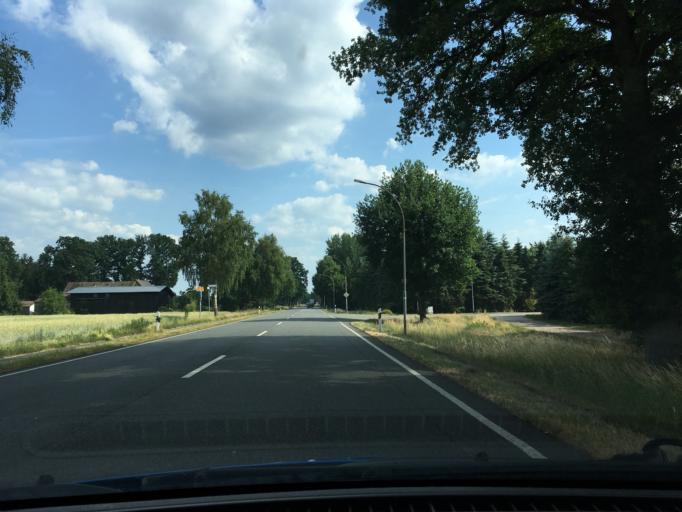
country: DE
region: Lower Saxony
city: Handeloh
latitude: 53.1908
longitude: 9.8318
